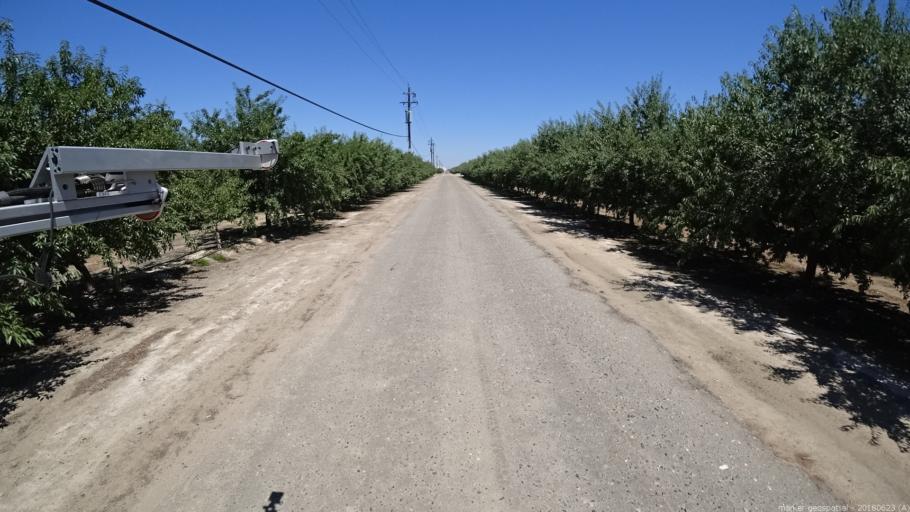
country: US
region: California
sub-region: Madera County
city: Fairmead
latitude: 37.0857
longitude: -120.2204
